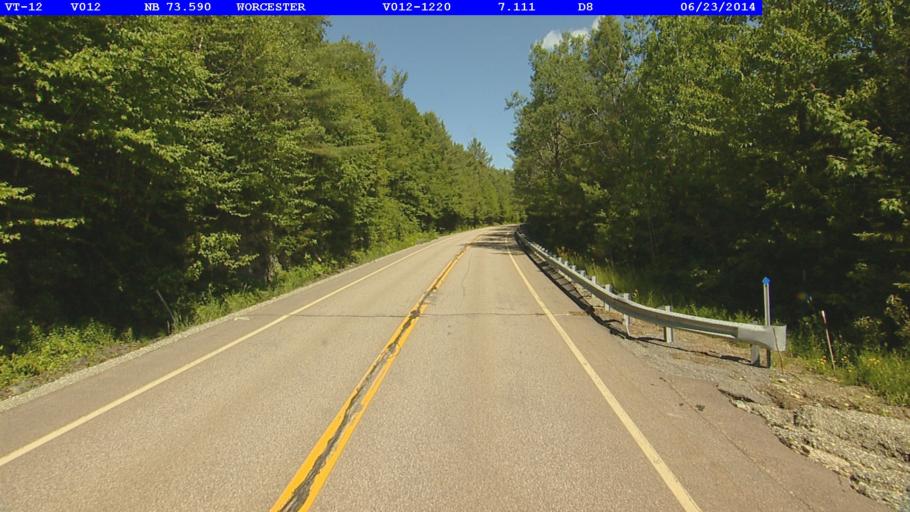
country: US
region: Vermont
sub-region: Lamoille County
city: Morrisville
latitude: 44.4420
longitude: -72.5417
